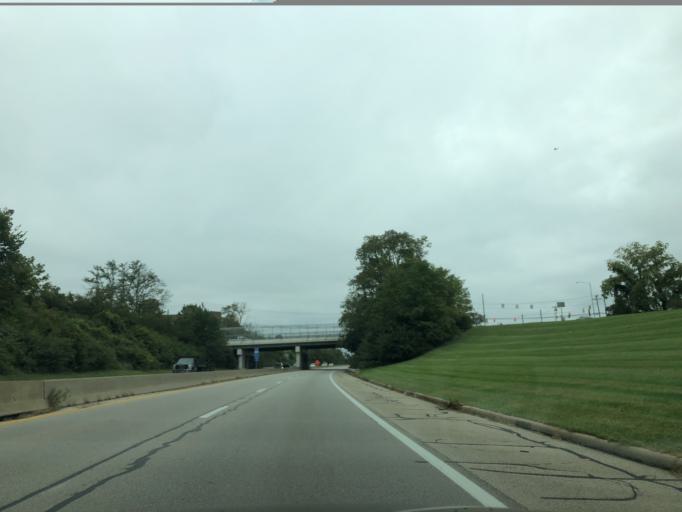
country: US
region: Ohio
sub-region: Hamilton County
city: Dillonvale
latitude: 39.2255
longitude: -84.3962
